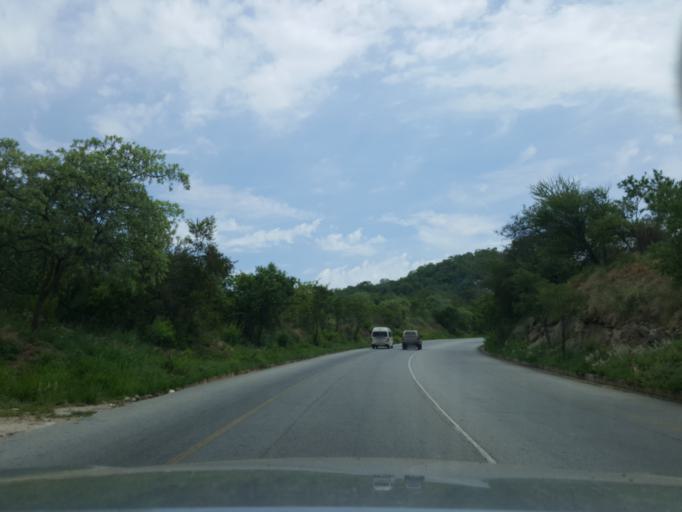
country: ZA
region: Mpumalanga
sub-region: Ehlanzeni District
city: Nelspruit
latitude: -25.4612
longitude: 31.0918
